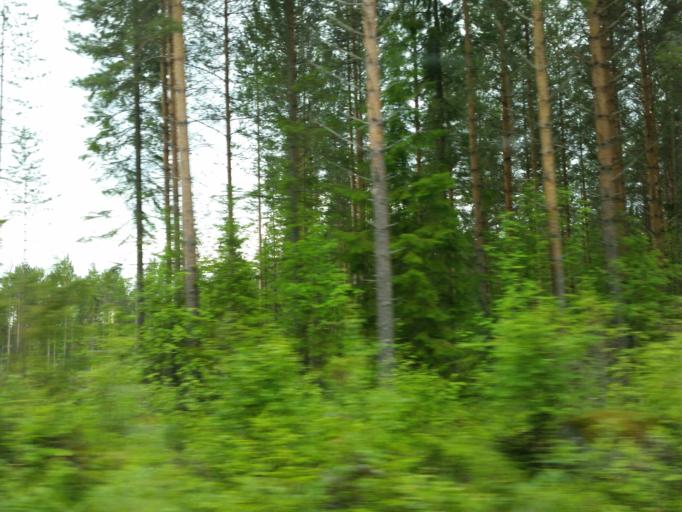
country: FI
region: Northern Savo
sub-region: Sisae-Savo
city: Tervo
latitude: 63.0724
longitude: 26.6033
